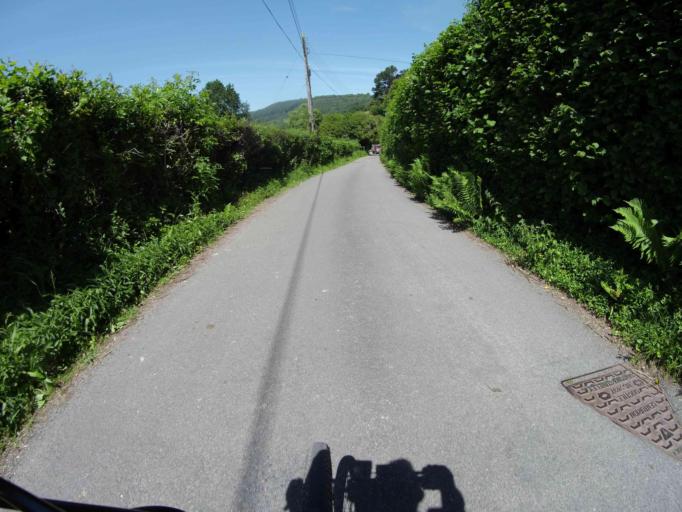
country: GB
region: England
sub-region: Devon
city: Bovey Tracey
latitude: 50.6168
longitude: -3.7134
